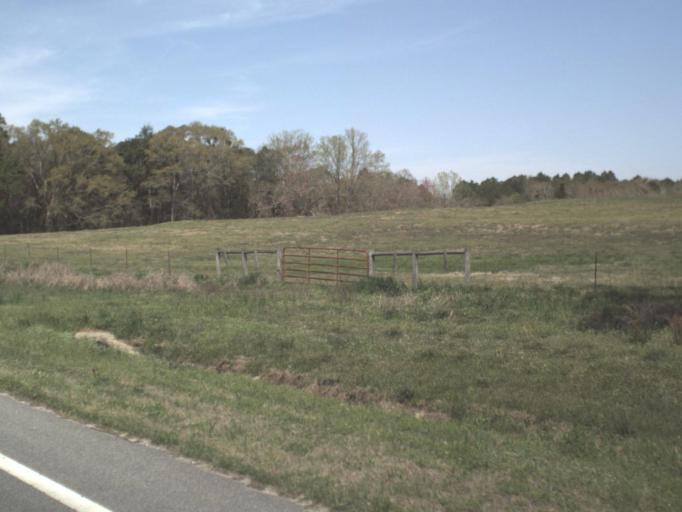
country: US
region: Florida
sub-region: Holmes County
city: Bonifay
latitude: 30.7901
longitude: -85.7035
